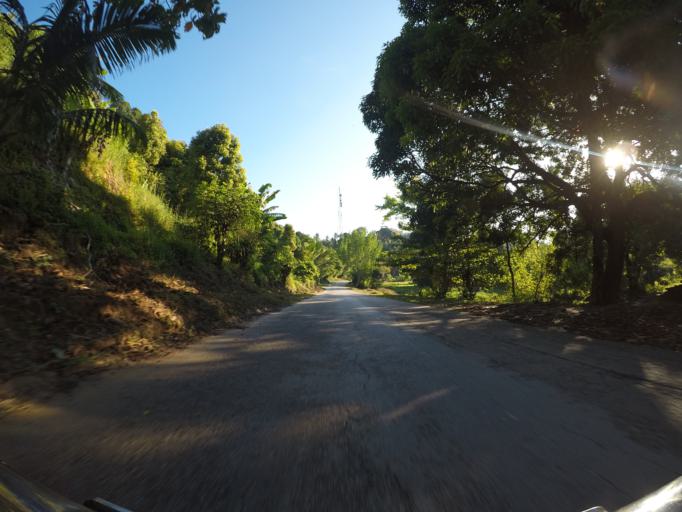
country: TZ
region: Pemba South
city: Mtambile
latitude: -5.3748
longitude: 39.6931
